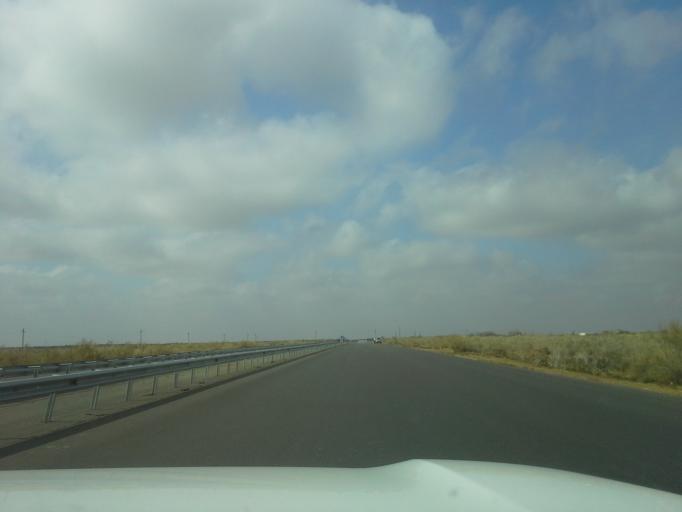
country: TM
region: Mary
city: Mary
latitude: 37.4212
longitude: 61.5750
